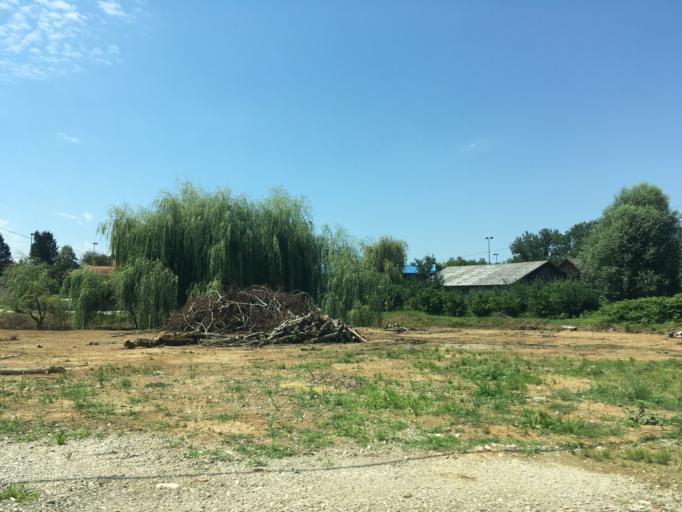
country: SI
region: Metlika
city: Metlika
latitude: 45.6326
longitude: 15.3234
